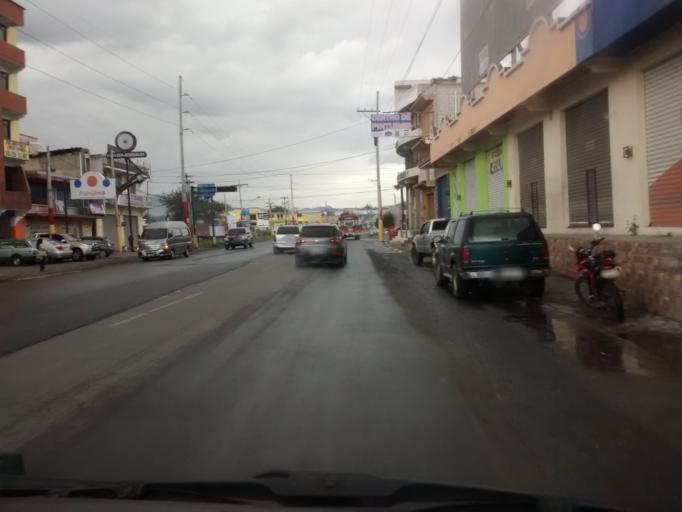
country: GT
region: Quetzaltenango
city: Olintepeque
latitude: 14.8598
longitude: -91.5219
